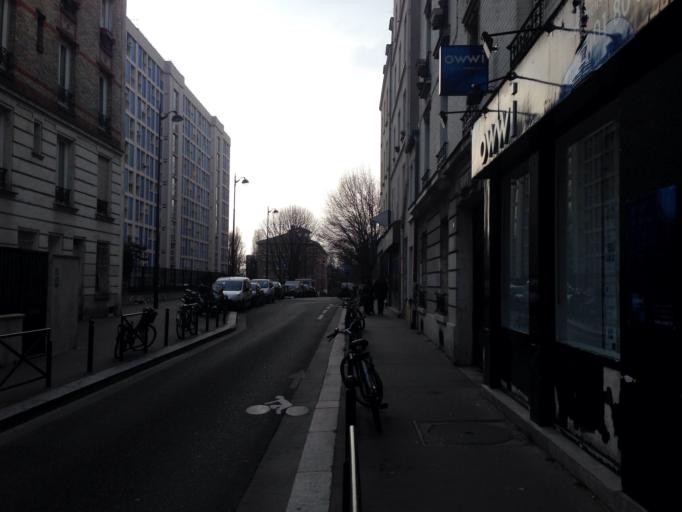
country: FR
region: Ile-de-France
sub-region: Departement de Seine-Saint-Denis
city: Le Pre-Saint-Gervais
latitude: 48.8781
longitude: 2.3848
